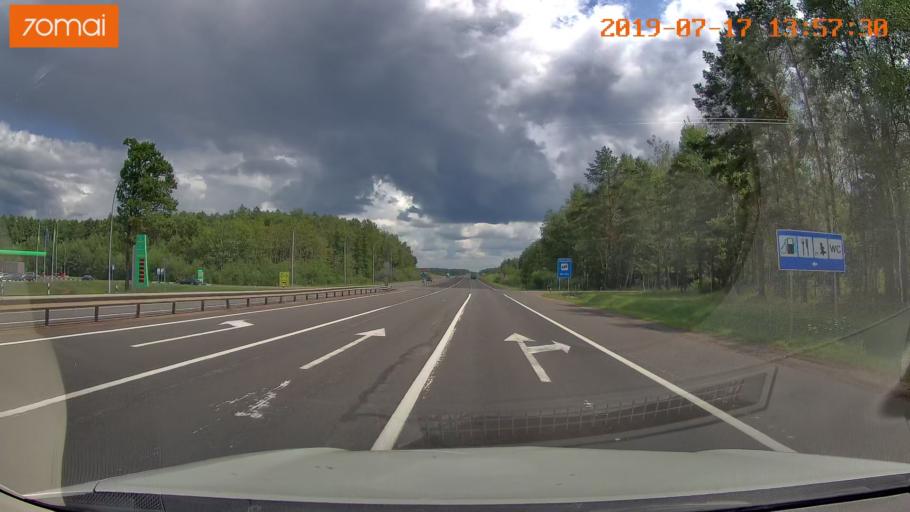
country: BY
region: Mogilev
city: Asipovichy
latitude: 53.3304
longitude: 28.6832
